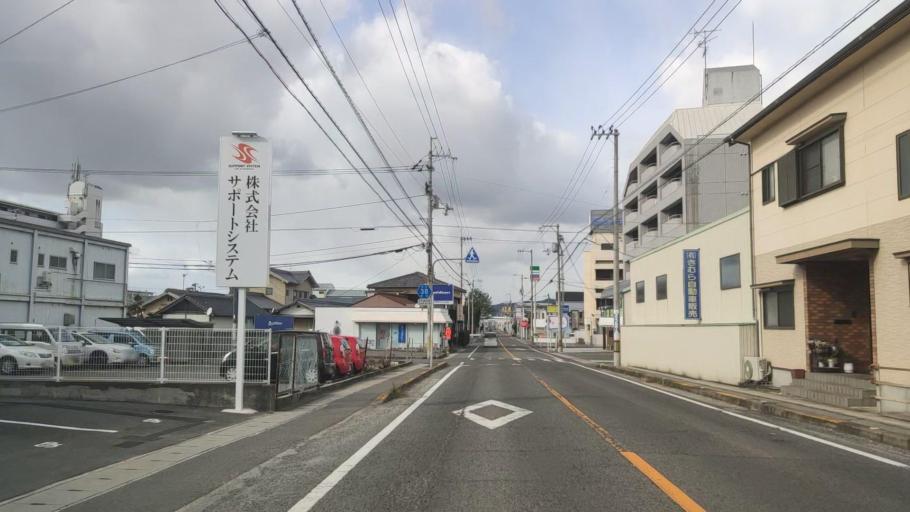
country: JP
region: Ehime
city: Saijo
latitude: 34.0485
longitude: 133.0169
